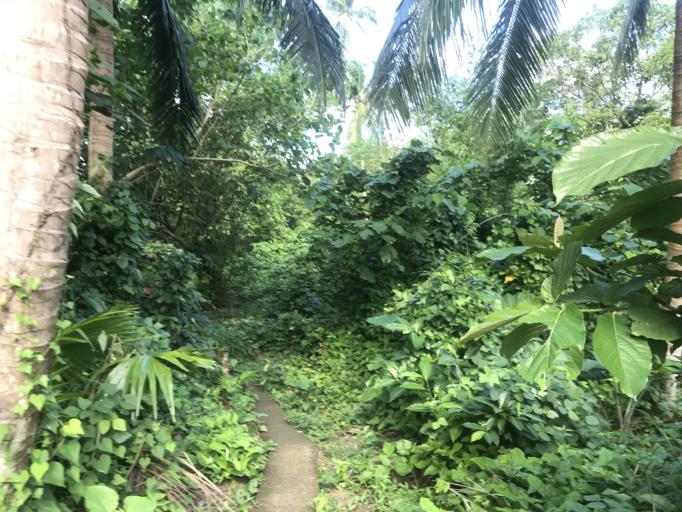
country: PH
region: Calabarzon
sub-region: Province of Quezon
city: Macalelon
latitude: 13.7826
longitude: 122.1405
